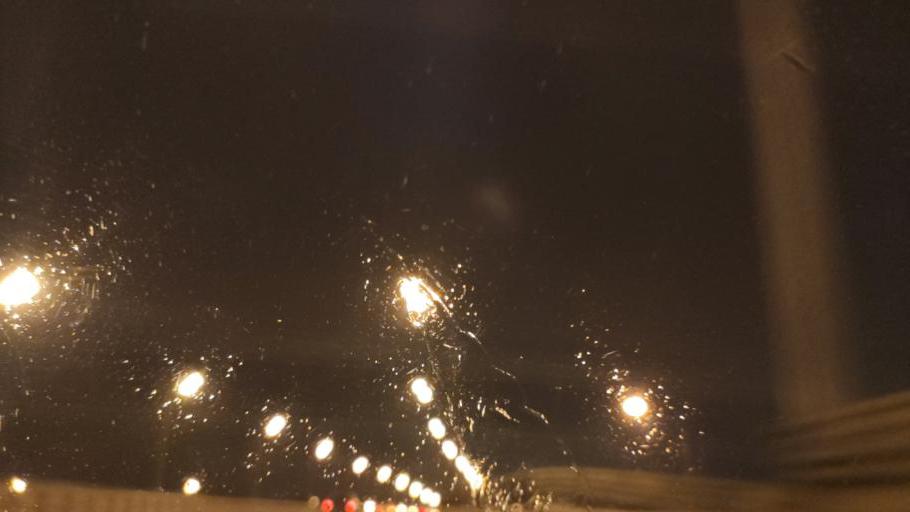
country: RU
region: Moscow
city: Vnukovo
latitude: 55.5939
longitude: 37.2363
